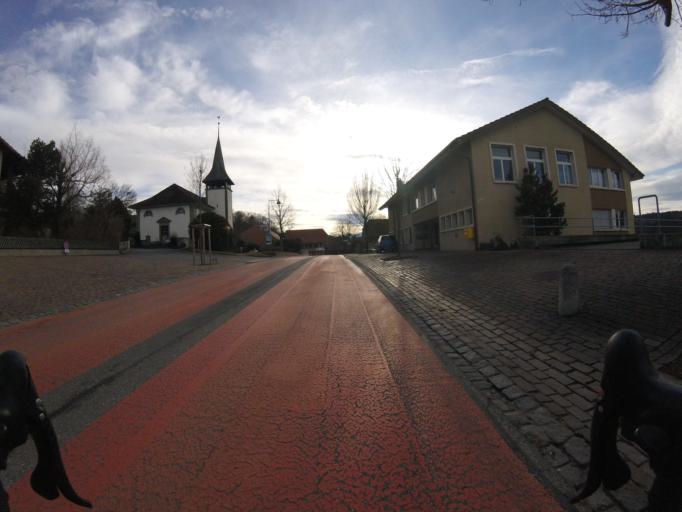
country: CH
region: Fribourg
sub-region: Sense District
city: Ueberstorf
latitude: 46.8519
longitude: 7.3183
